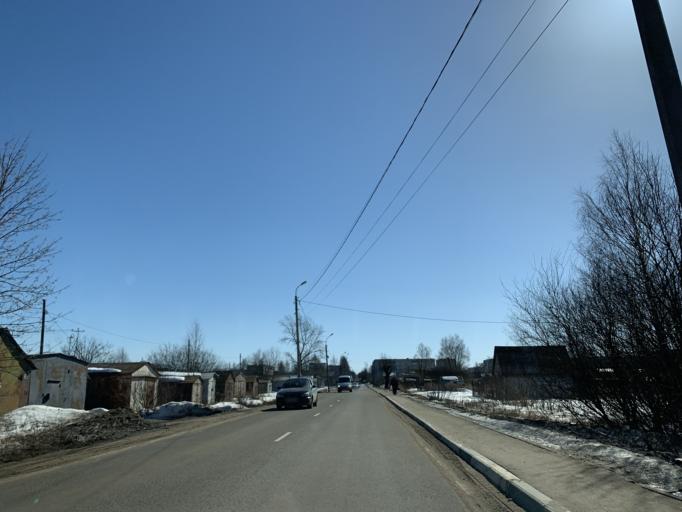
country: RU
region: Jaroslavl
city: Konstantinovskiy
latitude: 57.8353
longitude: 39.5881
